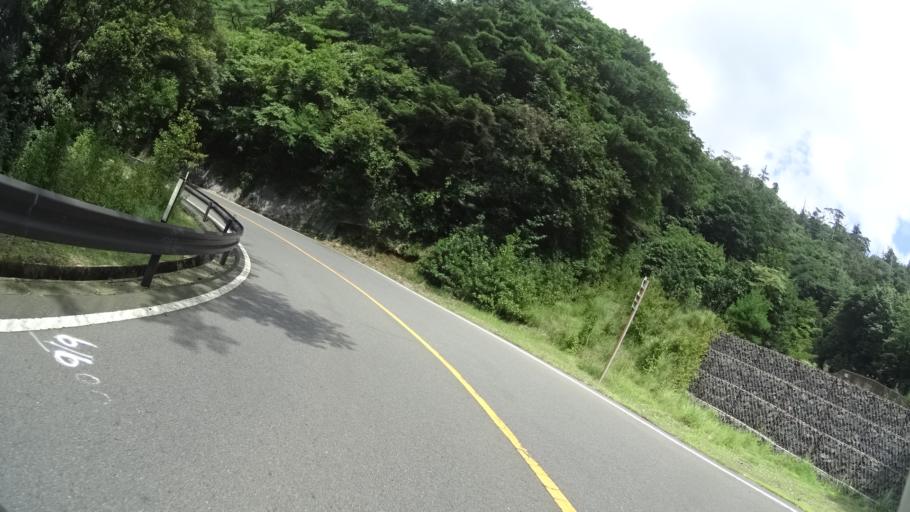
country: JP
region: Miyazaki
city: Kobayashi
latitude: 31.9043
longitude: 130.8461
